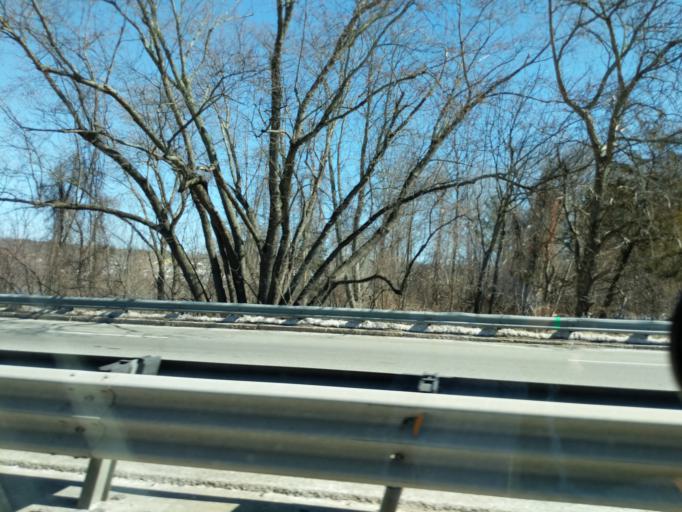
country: US
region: Rhode Island
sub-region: Providence County
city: Cumberland
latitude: 41.9222
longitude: -71.4566
